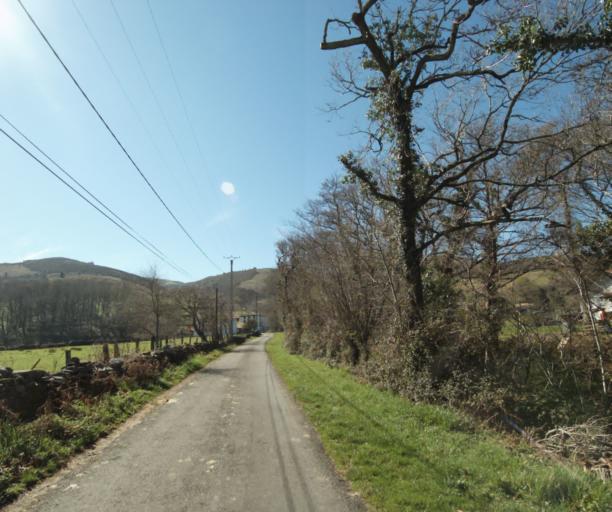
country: FR
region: Aquitaine
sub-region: Departement des Pyrenees-Atlantiques
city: Urrugne
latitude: 43.3372
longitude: -1.6966
